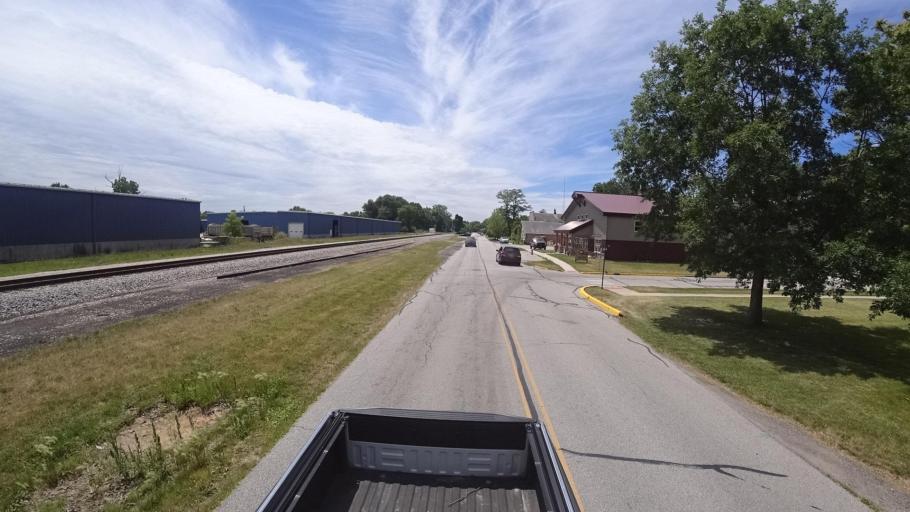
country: US
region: Indiana
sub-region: Porter County
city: Porter
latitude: 41.6168
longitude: -87.0701
